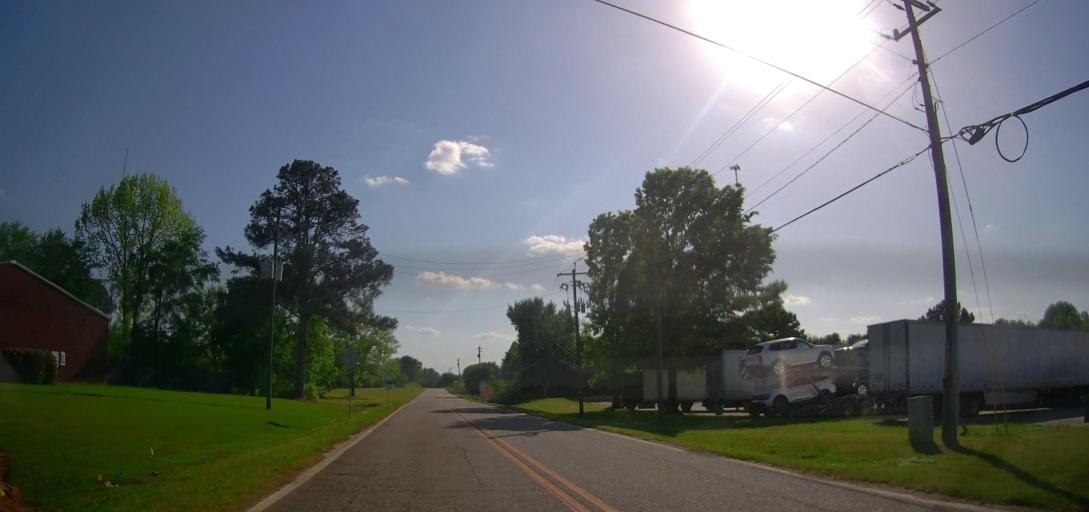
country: US
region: Georgia
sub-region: Morgan County
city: Madison
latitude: 33.5504
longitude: -83.4755
